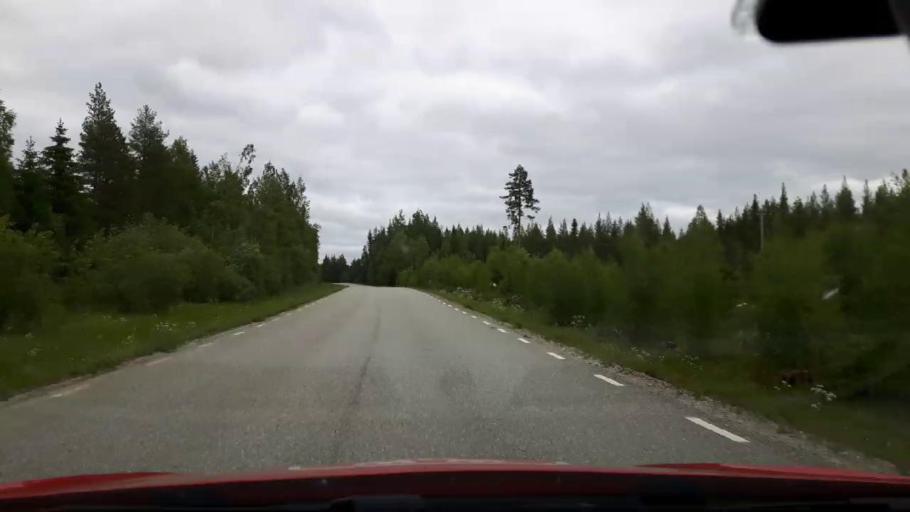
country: SE
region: Jaemtland
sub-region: Ragunda Kommun
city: Hammarstrand
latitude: 63.2097
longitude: 16.0053
